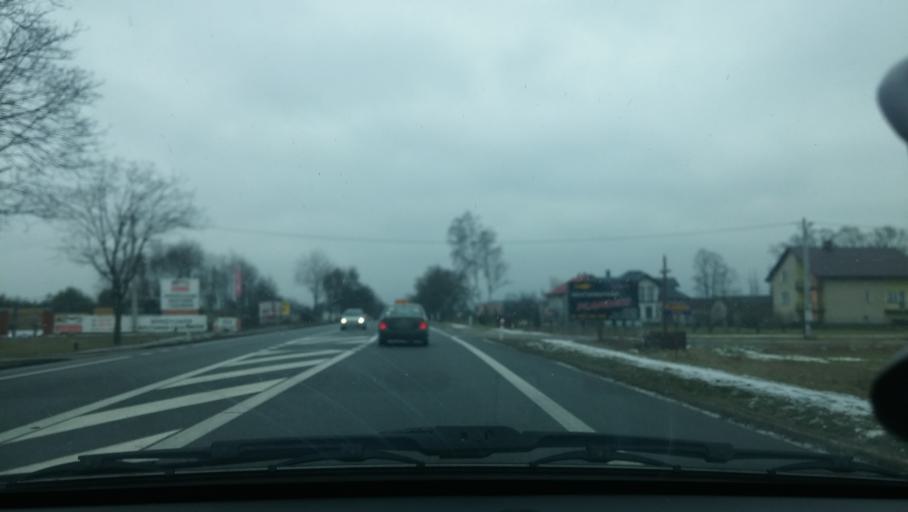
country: PL
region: Masovian Voivodeship
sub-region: Powiat siedlecki
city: Kotun
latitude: 52.1957
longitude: 22.0690
